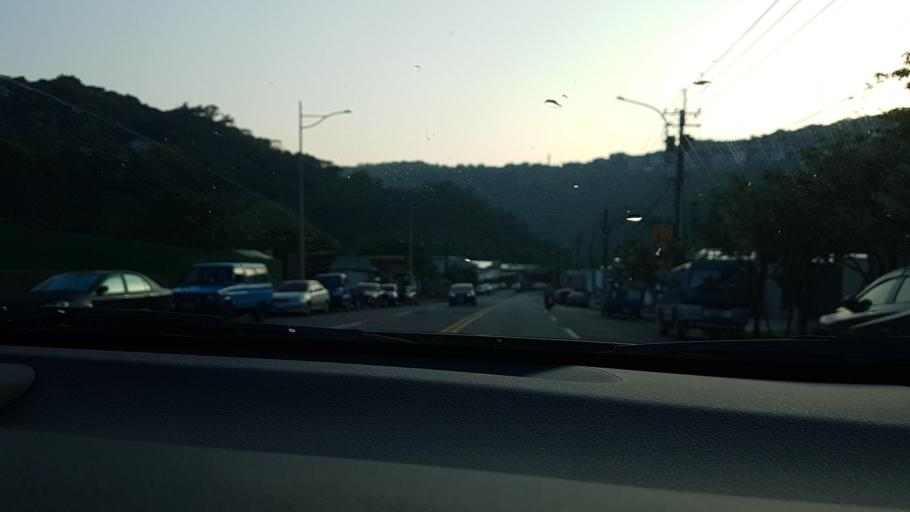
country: TW
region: Taipei
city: Taipei
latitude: 25.1128
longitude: 121.5640
